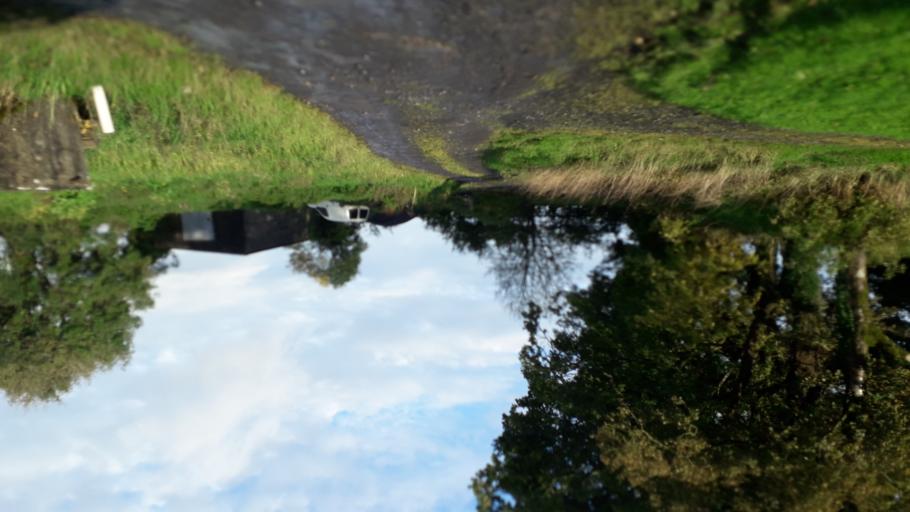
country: IE
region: Connaught
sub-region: Roscommon
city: Roscommon
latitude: 53.7725
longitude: -8.2289
